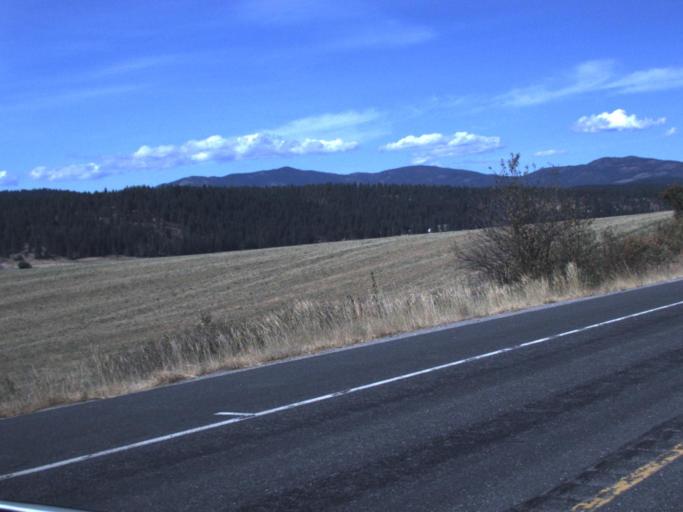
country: US
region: Washington
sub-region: Stevens County
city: Colville
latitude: 48.4328
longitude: -117.8607
